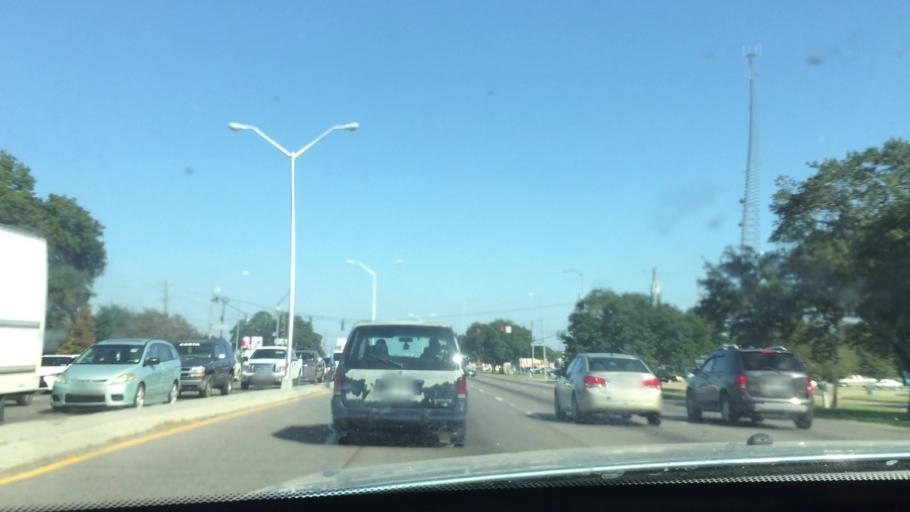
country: US
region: Louisiana
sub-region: East Baton Rouge Parish
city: Baton Rouge
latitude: 30.4516
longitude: -91.1134
